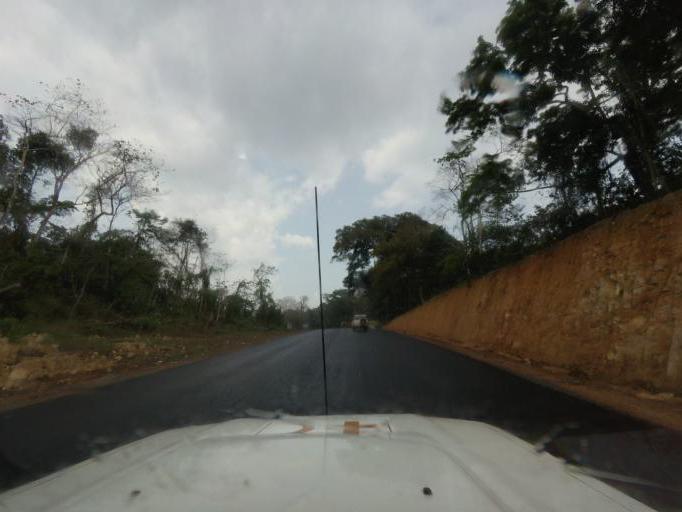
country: LR
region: Margibi
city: Kakata
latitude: 6.7783
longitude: -9.9762
